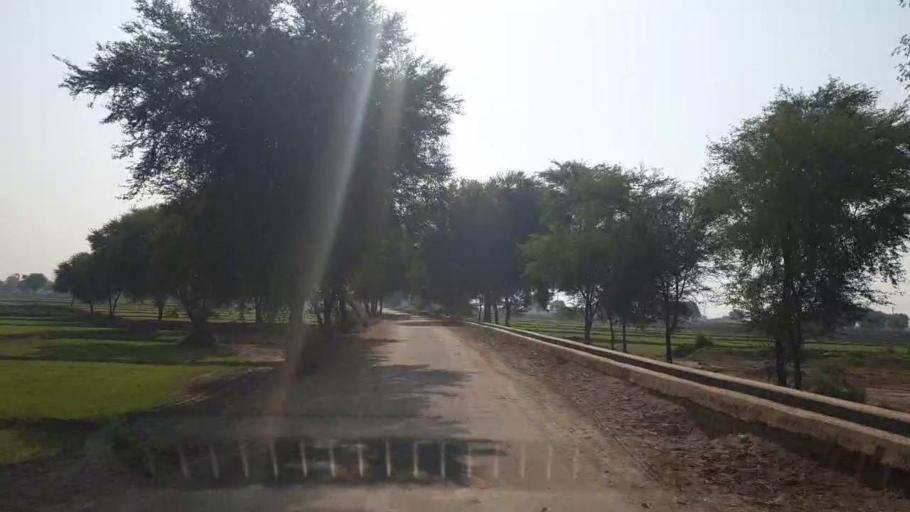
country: PK
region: Sindh
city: Sehwan
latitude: 26.4410
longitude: 67.8396
